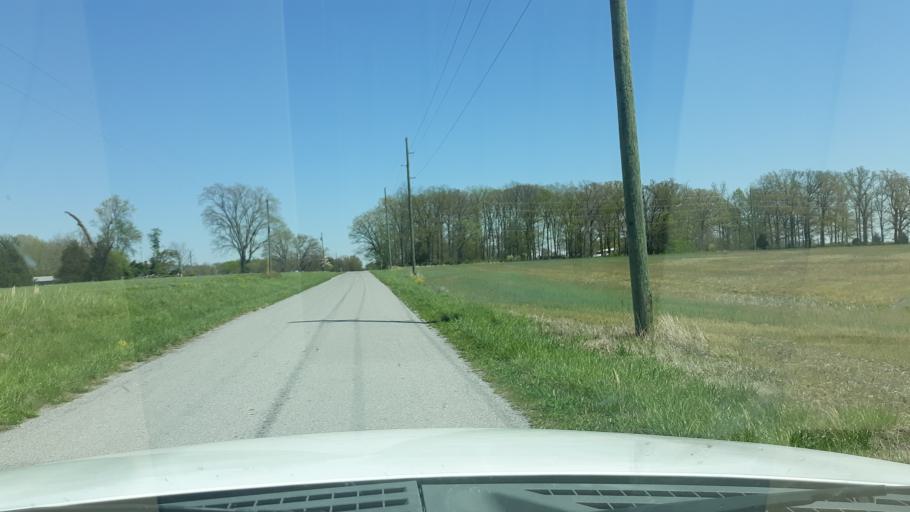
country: US
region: Illinois
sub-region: Saline County
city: Harrisburg
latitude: 37.8850
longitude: -88.6677
